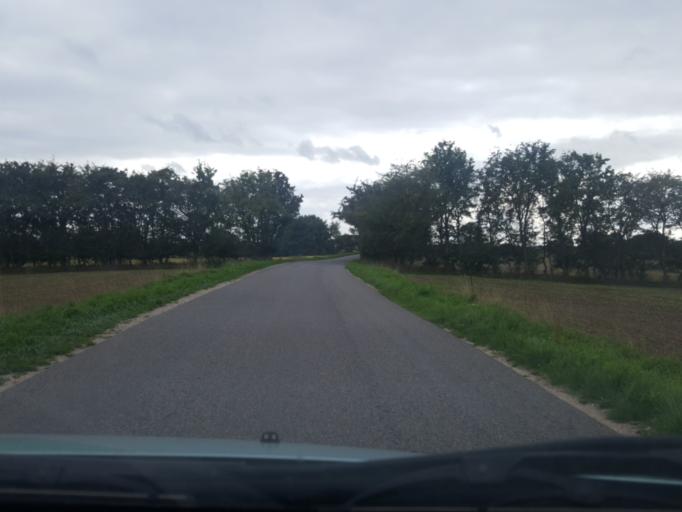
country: DK
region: Zealand
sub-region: Soro Kommune
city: Soro
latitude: 55.4692
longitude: 11.5199
